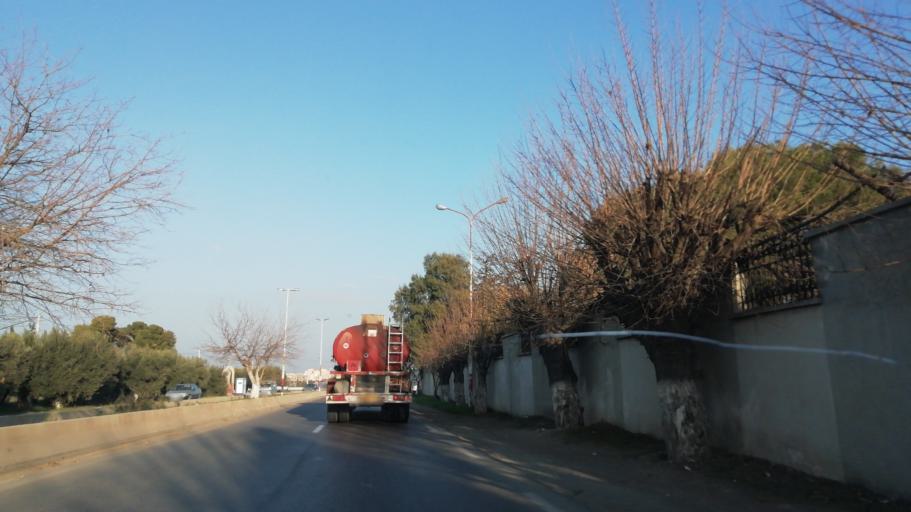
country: DZ
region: Sidi Bel Abbes
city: Sidi Bel Abbes
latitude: 35.1811
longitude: -0.6601
